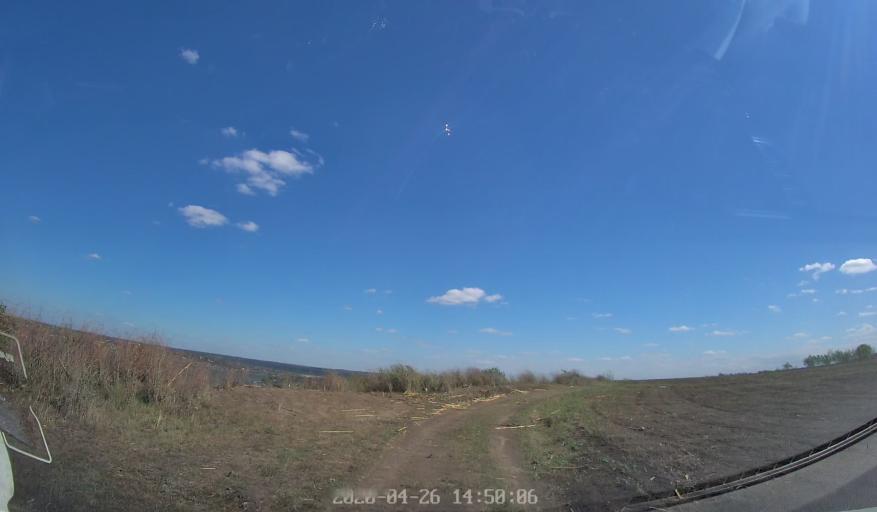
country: MD
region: Telenesti
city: Cocieri
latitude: 47.3586
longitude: 29.0649
